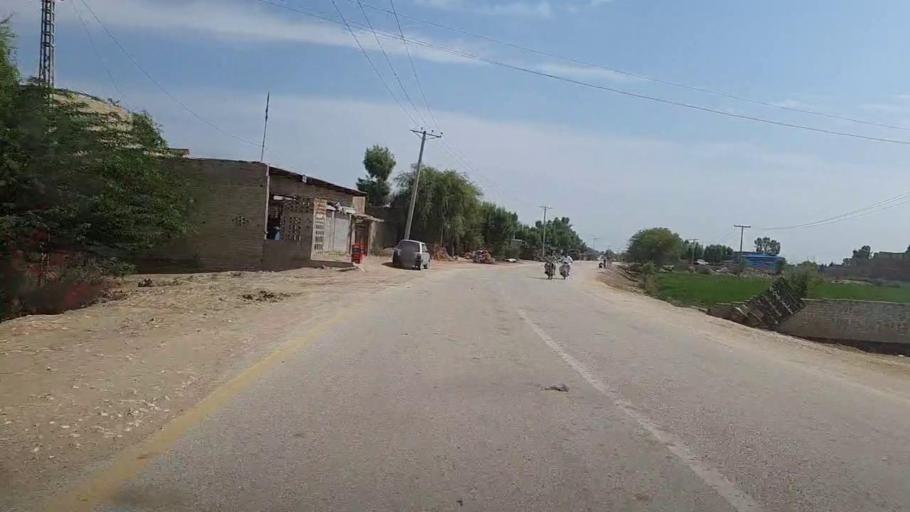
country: PK
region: Sindh
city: Thul
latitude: 28.2391
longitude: 68.7893
